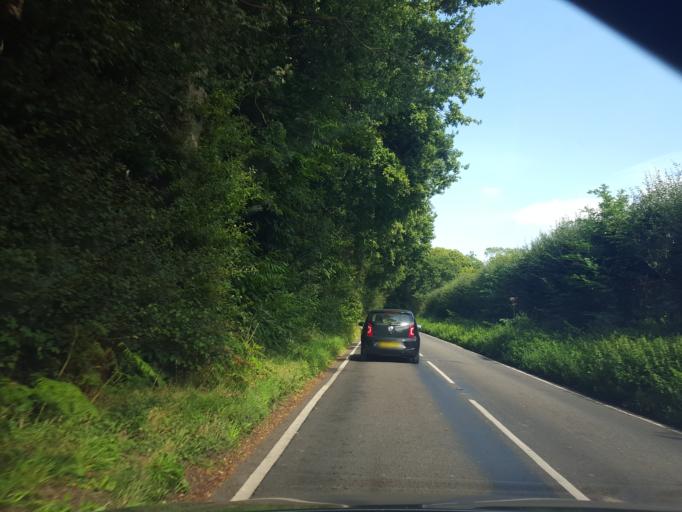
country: GB
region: England
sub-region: Suffolk
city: Shotley Gate
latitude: 51.9327
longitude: 1.1806
